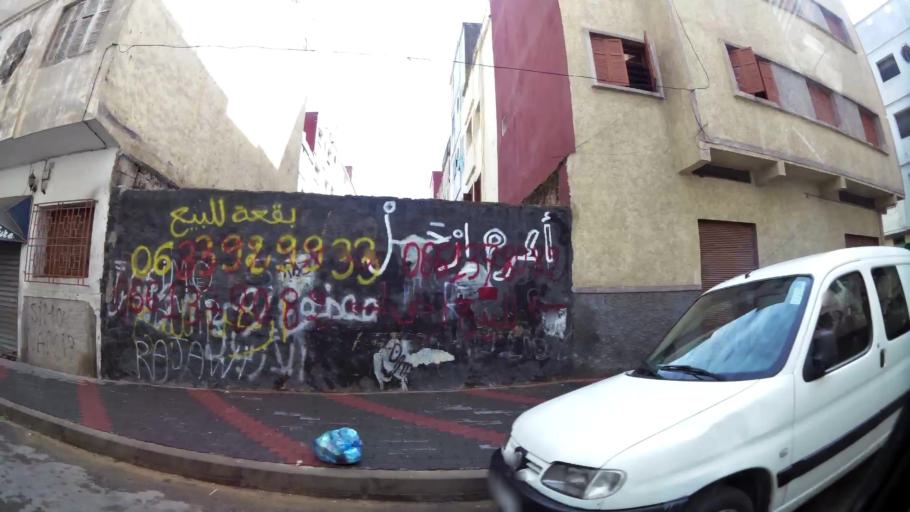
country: MA
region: Grand Casablanca
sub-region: Casablanca
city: Casablanca
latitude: 33.5695
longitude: -7.5913
